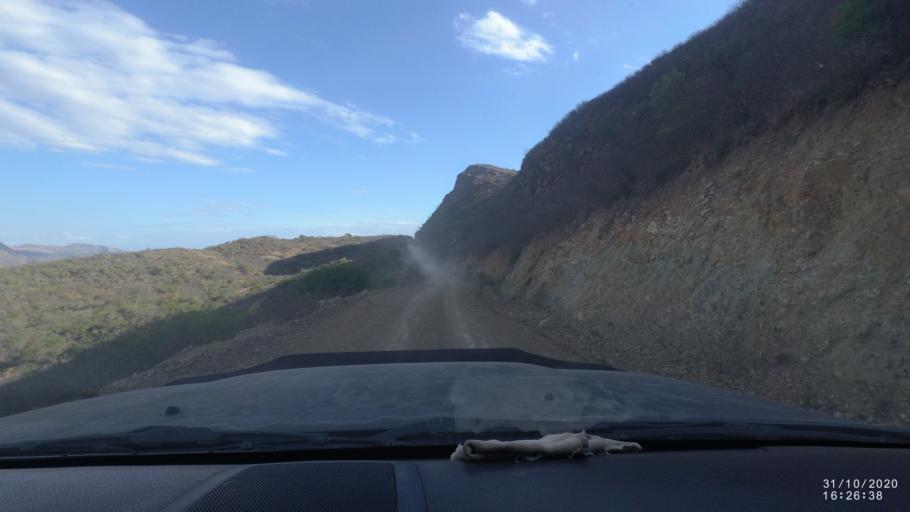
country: BO
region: Chuquisaca
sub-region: Provincia Zudanez
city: Mojocoya
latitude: -18.3997
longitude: -64.5862
